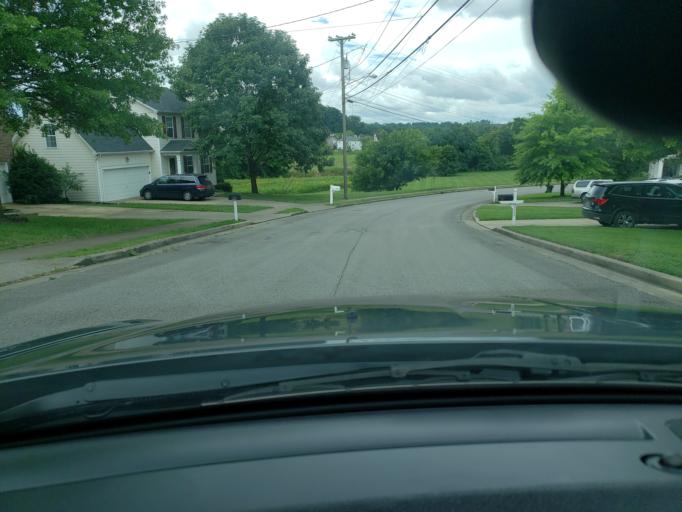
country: US
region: Tennessee
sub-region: Williamson County
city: Nolensville
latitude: 36.0221
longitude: -86.6861
